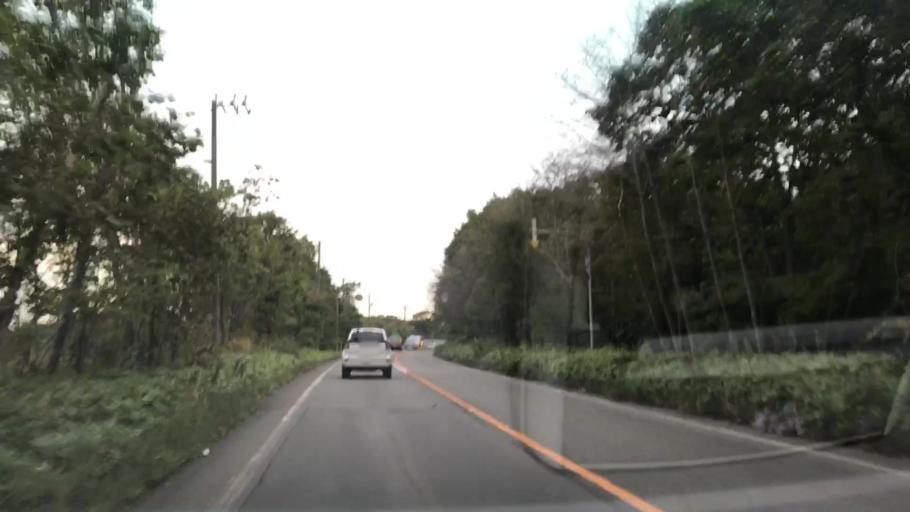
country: JP
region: Hokkaido
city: Tomakomai
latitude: 42.7060
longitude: 141.6635
